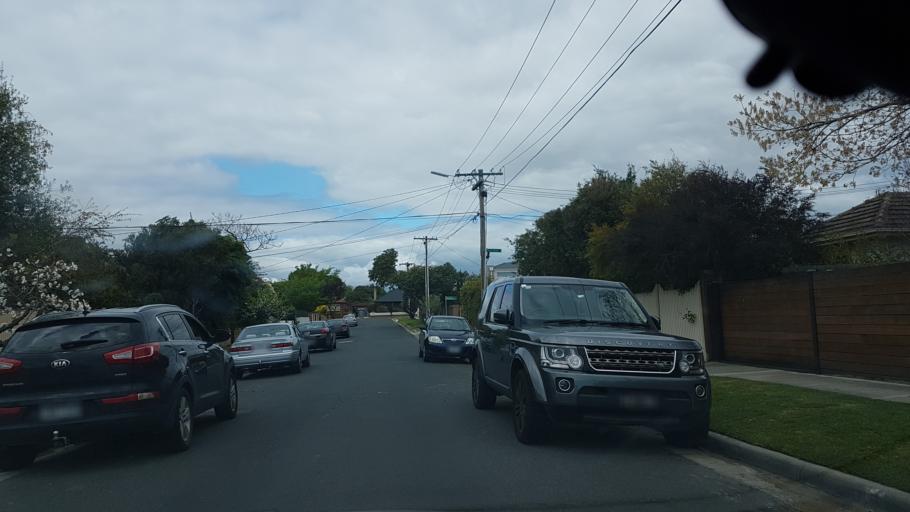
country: AU
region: Victoria
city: McKinnon
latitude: -37.9256
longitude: 145.0473
